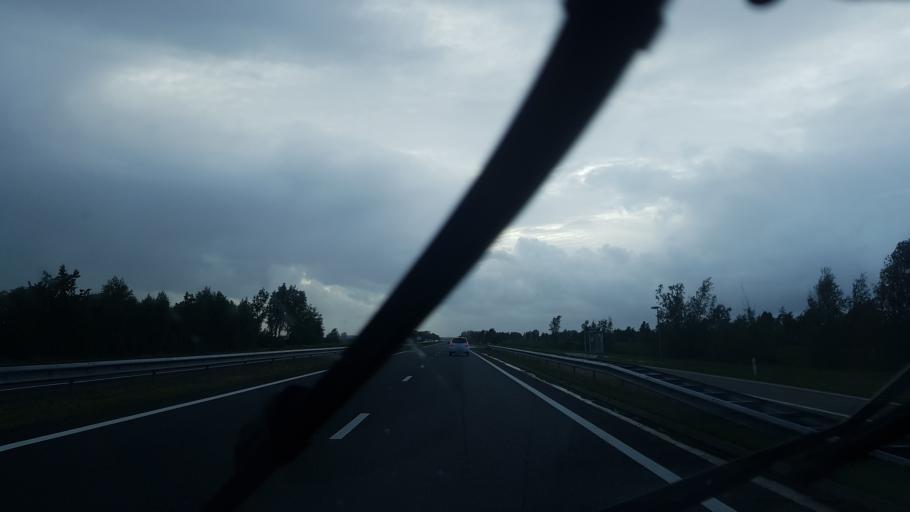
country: NL
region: Friesland
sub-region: Gemeente Tytsjerksteradiel
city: Garyp
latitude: 53.1545
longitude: 5.9694
